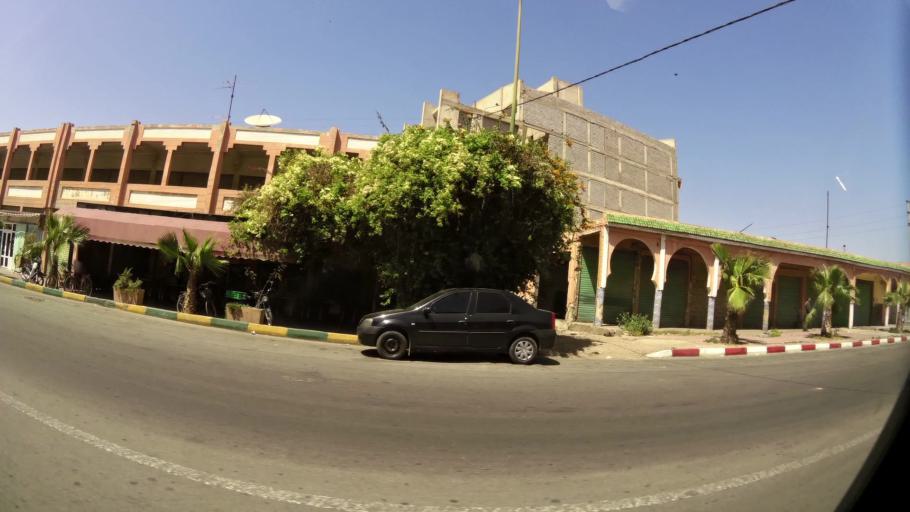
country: MA
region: Souss-Massa-Draa
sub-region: Inezgane-Ait Mellou
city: Inezgane
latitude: 30.3489
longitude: -9.5064
